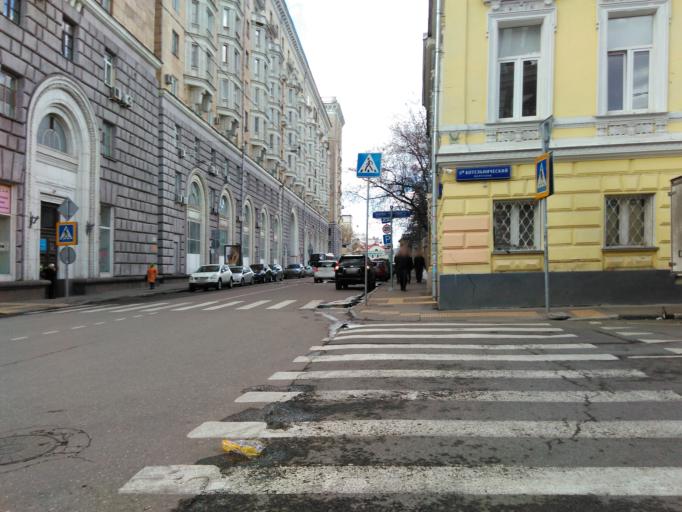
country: RU
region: Moscow
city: Taganskiy
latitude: 55.7422
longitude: 37.6502
